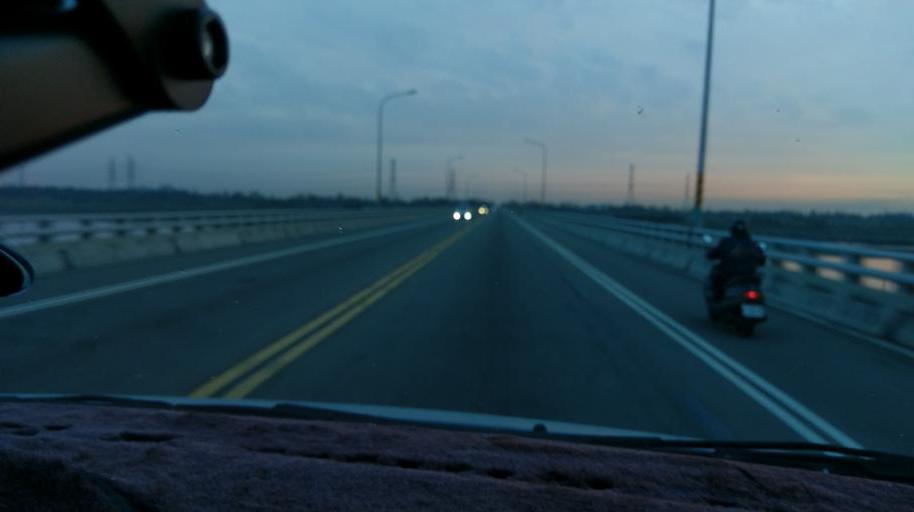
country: TW
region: Taiwan
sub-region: Changhua
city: Chang-hua
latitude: 24.1912
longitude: 120.5080
